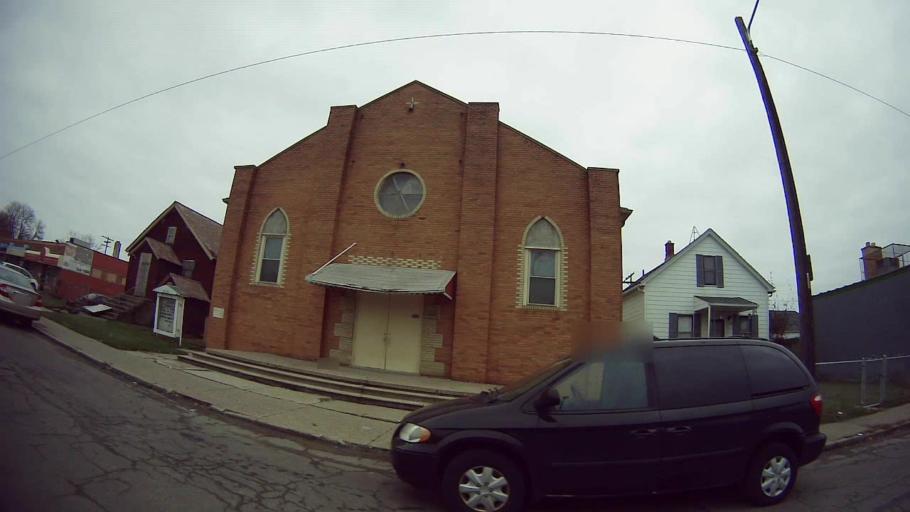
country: US
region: Michigan
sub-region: Wayne County
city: Hamtramck
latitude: 42.4078
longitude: -83.0563
